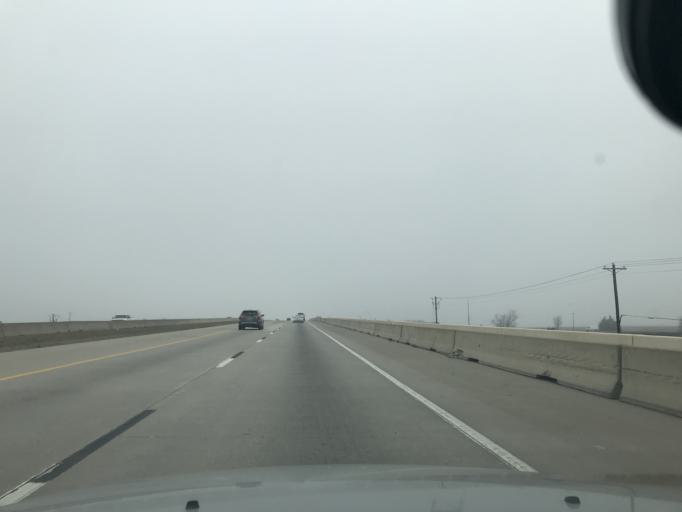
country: US
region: Texas
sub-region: Rockwall County
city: Fate
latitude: 32.9359
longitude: -96.3785
